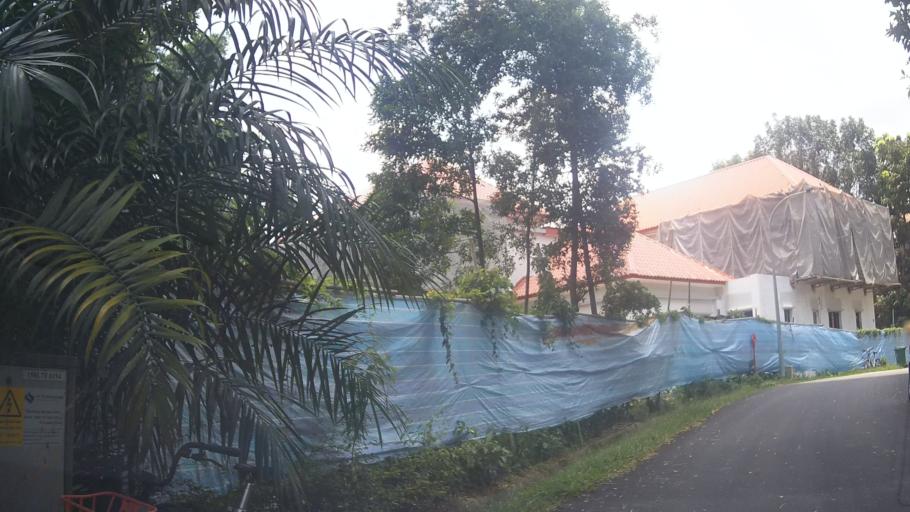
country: SG
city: Singapore
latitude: 1.3417
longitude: 103.7839
